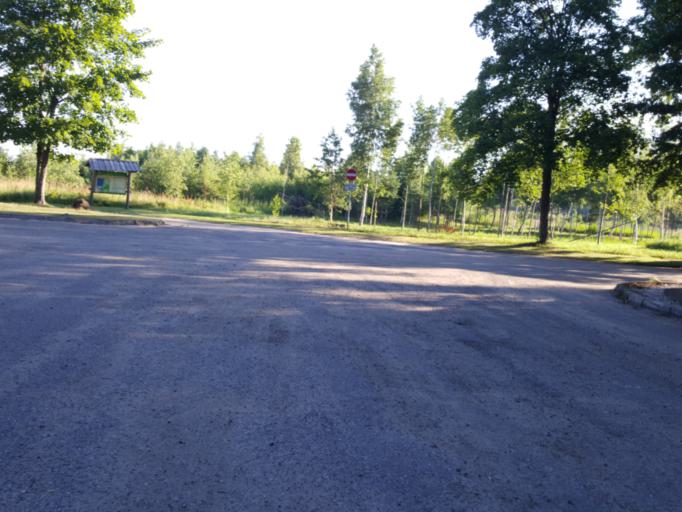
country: LV
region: Salacgrivas
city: Ainazi
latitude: 57.8660
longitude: 24.3565
